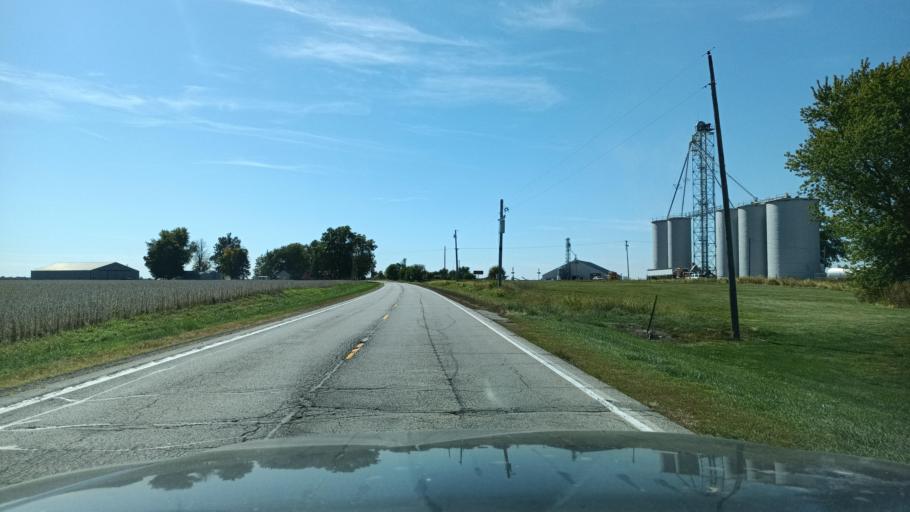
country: US
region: Illinois
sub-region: De Witt County
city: Farmer City
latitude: 40.2228
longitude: -88.7179
